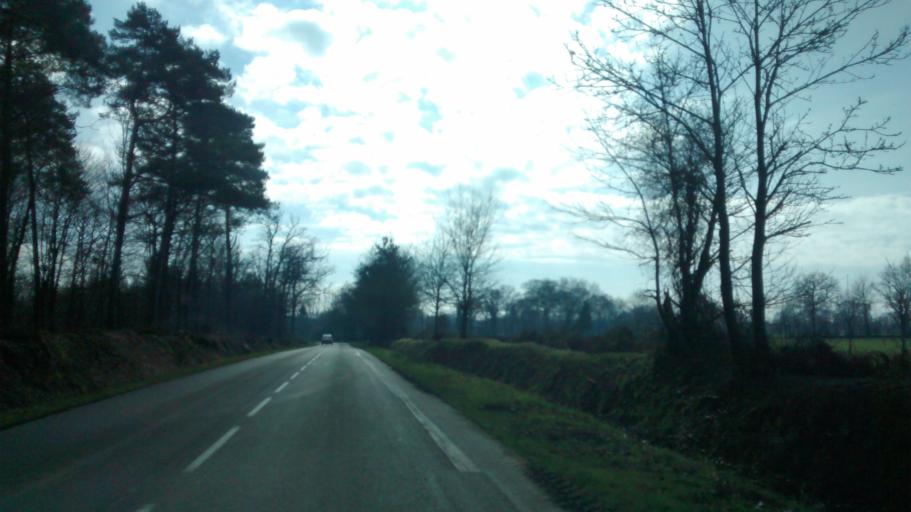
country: FR
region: Brittany
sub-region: Departement d'Ille-et-Vilaine
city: Fouillard
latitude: 48.1682
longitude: -1.5952
